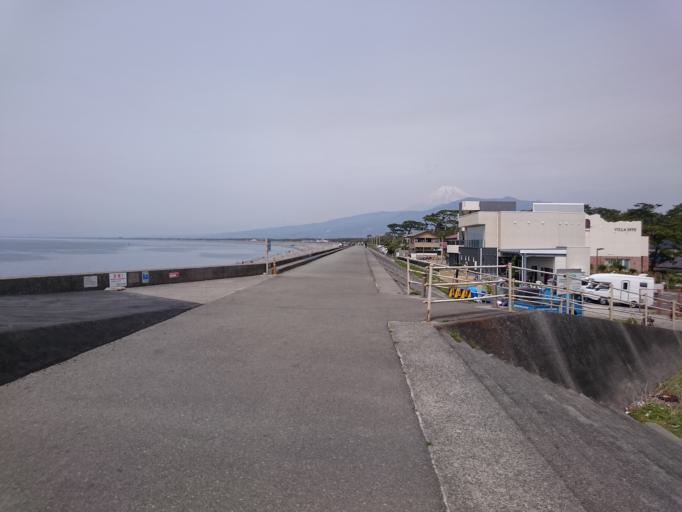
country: JP
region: Shizuoka
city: Numazu
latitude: 35.0898
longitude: 138.8495
